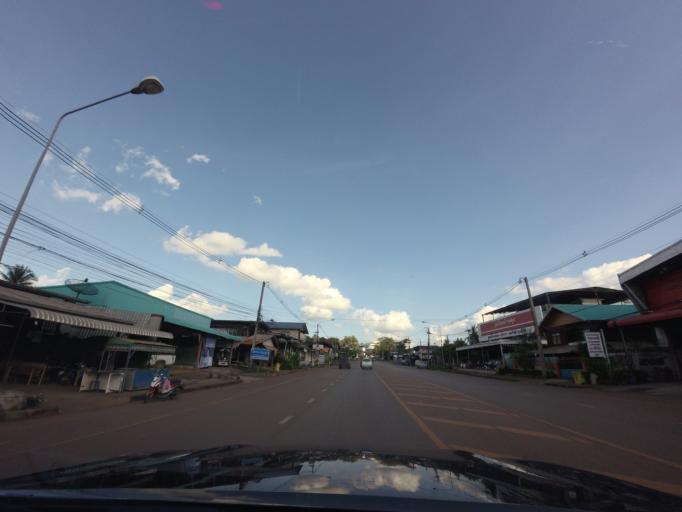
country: TH
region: Changwat Udon Thani
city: Ban Dung
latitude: 17.7026
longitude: 103.2560
